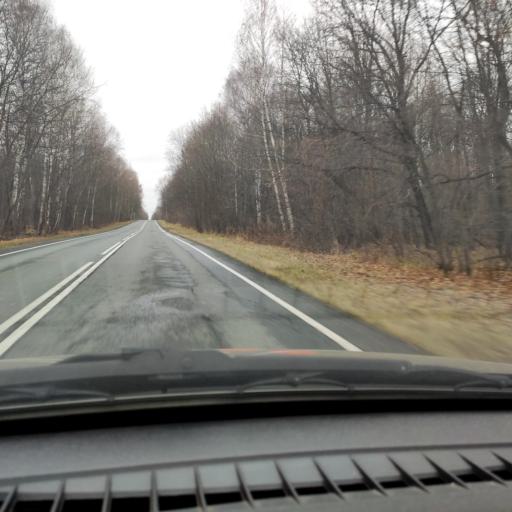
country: RU
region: Samara
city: Zhigulevsk
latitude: 53.3467
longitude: 49.5662
